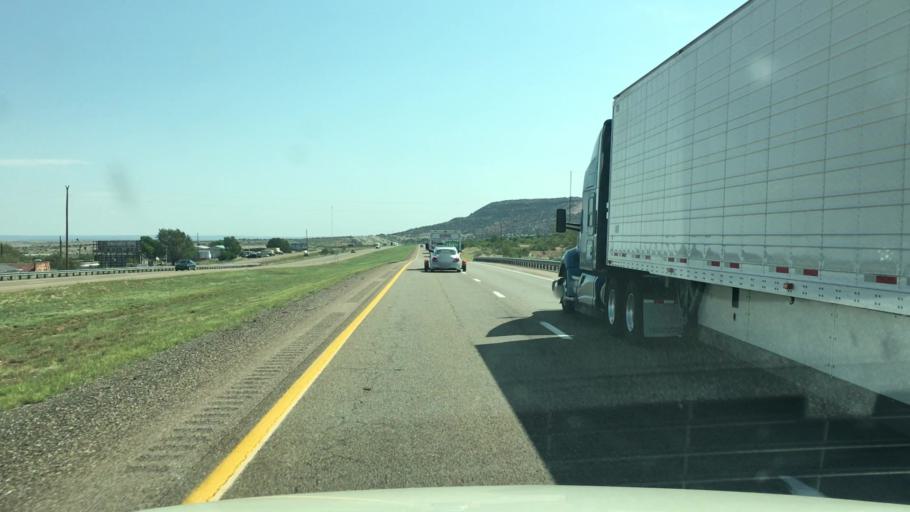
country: US
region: New Mexico
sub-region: Guadalupe County
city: Santa Rosa
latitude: 35.0306
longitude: -104.4108
